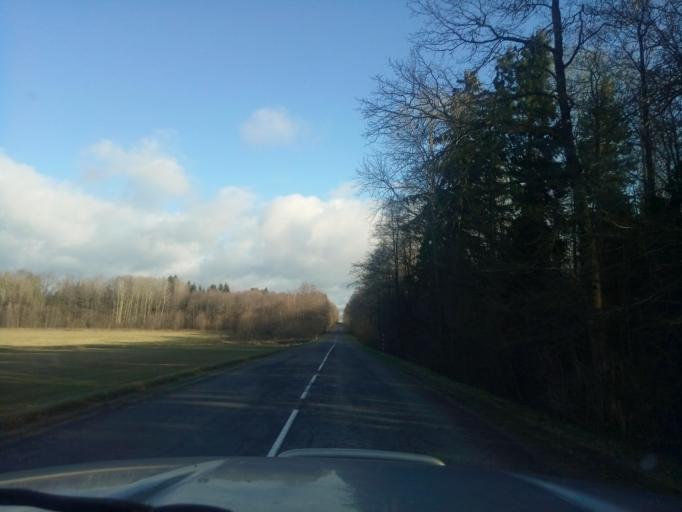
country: BY
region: Minsk
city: Tsimkavichy
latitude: 53.1696
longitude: 26.9233
